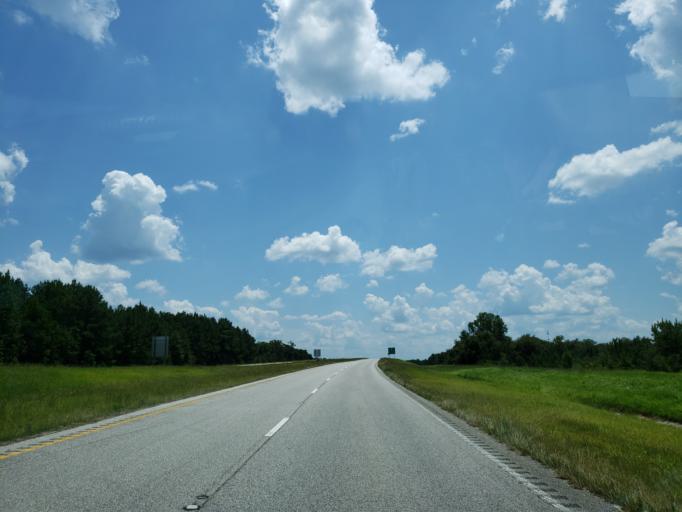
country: US
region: Mississippi
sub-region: Wayne County
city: Belmont
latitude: 31.4504
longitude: -88.4651
